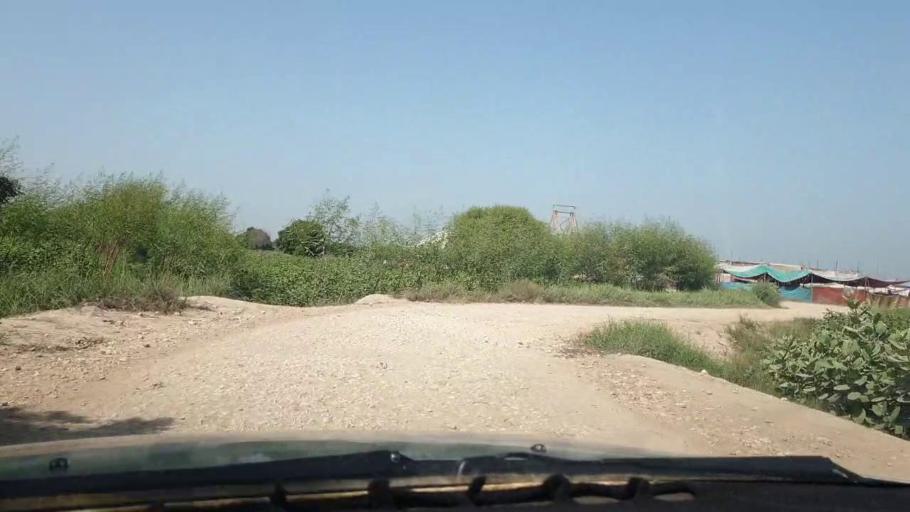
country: PK
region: Sindh
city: Chambar
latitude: 25.2305
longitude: 68.8686
